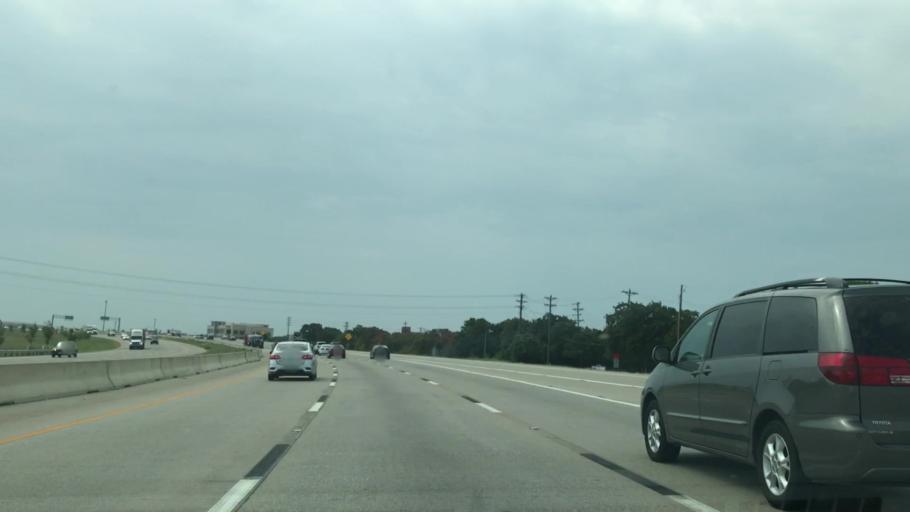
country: US
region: Texas
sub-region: Tarrant County
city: Southlake
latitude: 32.9645
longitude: -97.1561
